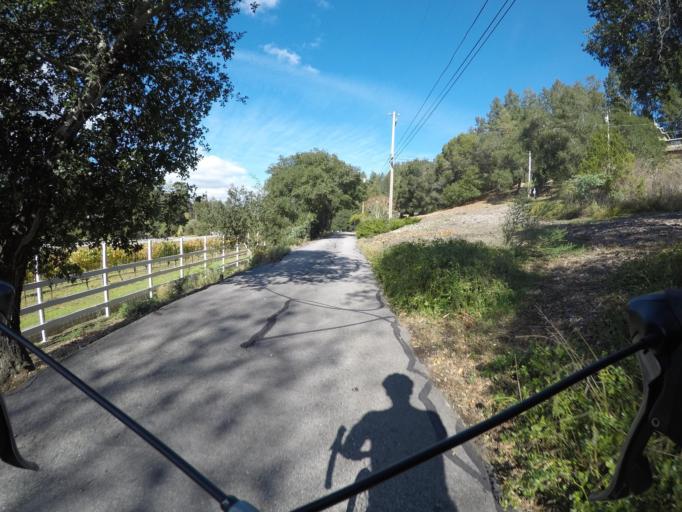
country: US
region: California
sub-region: Santa Cruz County
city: Pasatiempo
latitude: 37.0191
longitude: -122.0199
